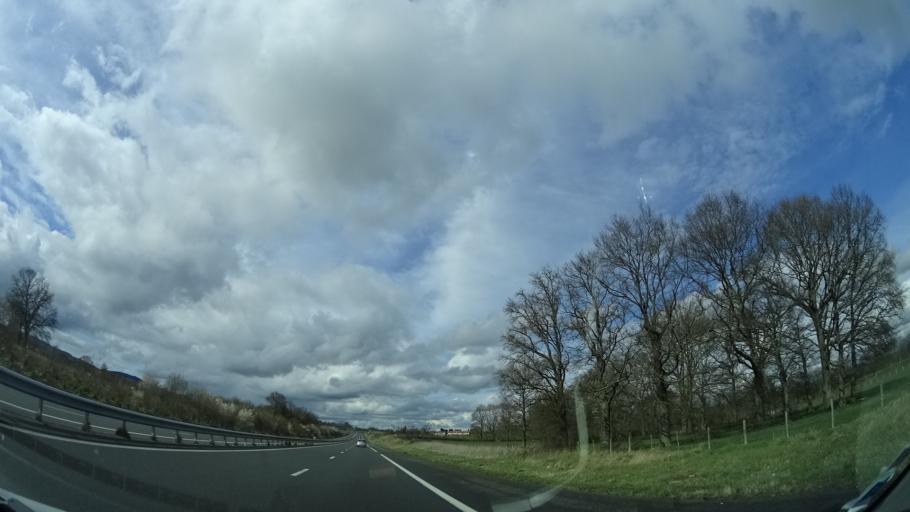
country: FR
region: Rhone-Alpes
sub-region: Departement de la Loire
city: La Pacaudiere
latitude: 46.1644
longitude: 3.8879
